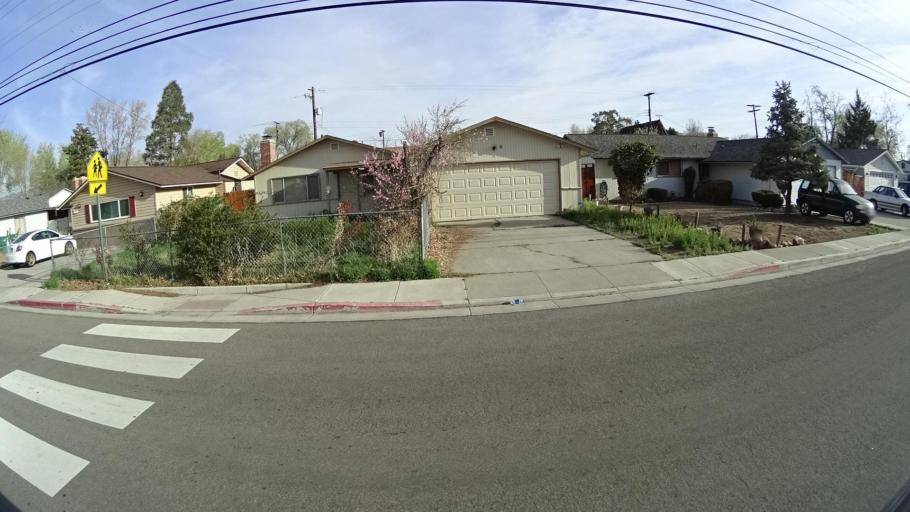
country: US
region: Nevada
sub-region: Washoe County
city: Reno
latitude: 39.5075
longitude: -119.7956
